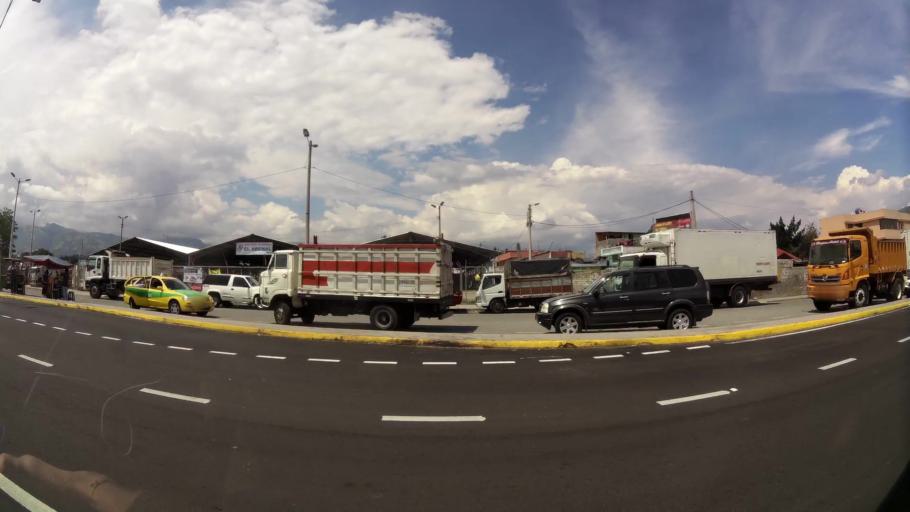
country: EC
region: Pichincha
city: Sangolqui
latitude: -0.2044
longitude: -78.3774
